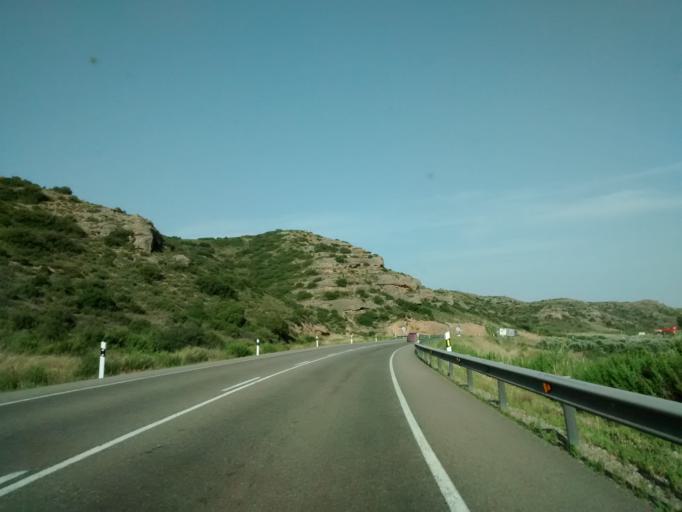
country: ES
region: Aragon
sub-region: Provincia de Zaragoza
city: Bulbuente
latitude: 41.8262
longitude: -1.6419
